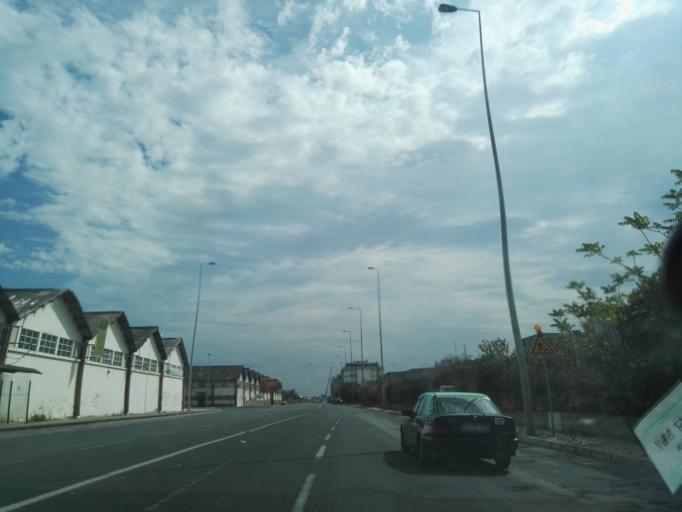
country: PT
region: Lisbon
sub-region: Loures
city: Moscavide
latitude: 38.7512
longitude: -9.0960
